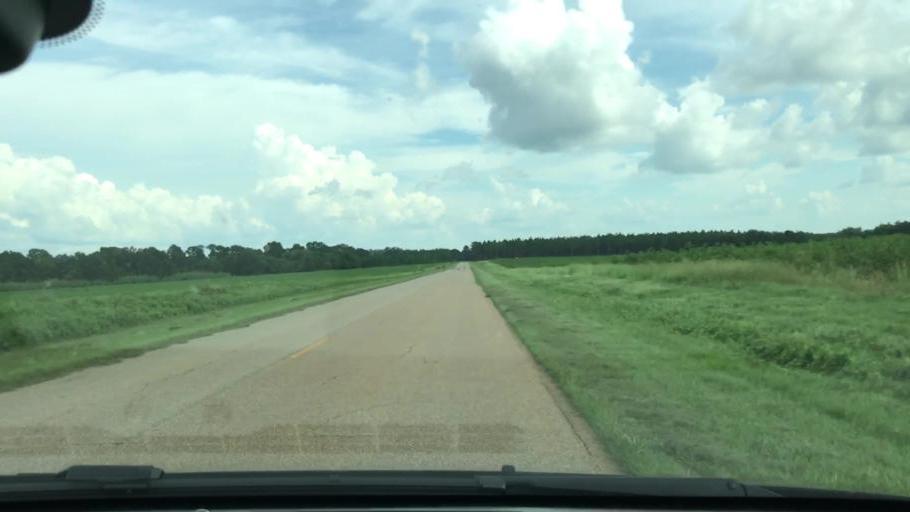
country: US
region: Georgia
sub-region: Clay County
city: Fort Gaines
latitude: 31.5654
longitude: -84.9877
